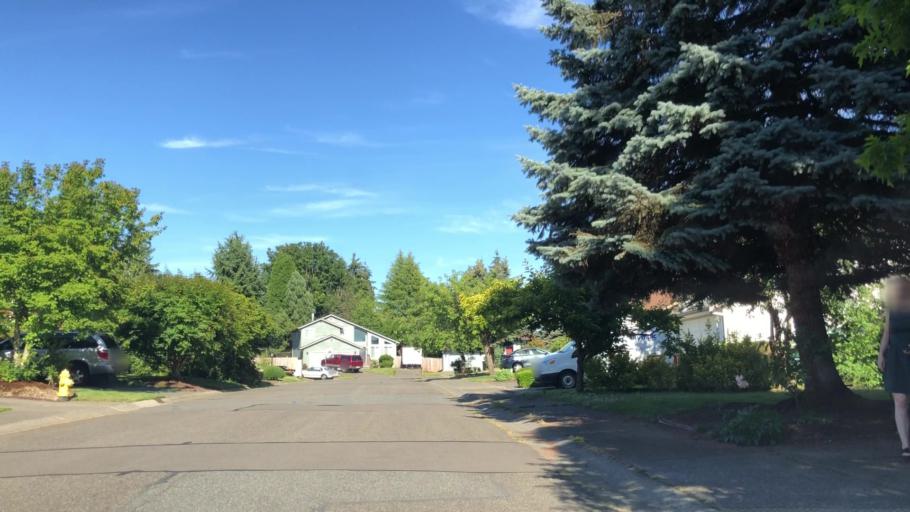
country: US
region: Washington
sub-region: King County
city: Kingsgate
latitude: 47.7200
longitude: -122.1702
